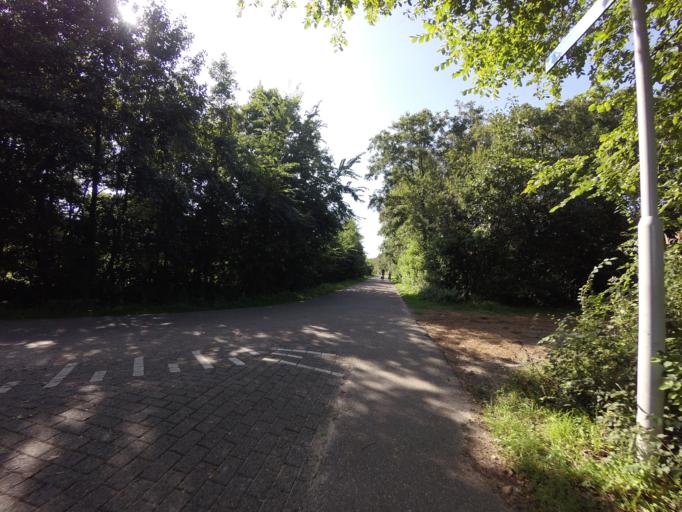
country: NL
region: Friesland
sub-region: Gemeente Terschelling
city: West-Terschelling
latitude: 53.3913
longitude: 5.2926
